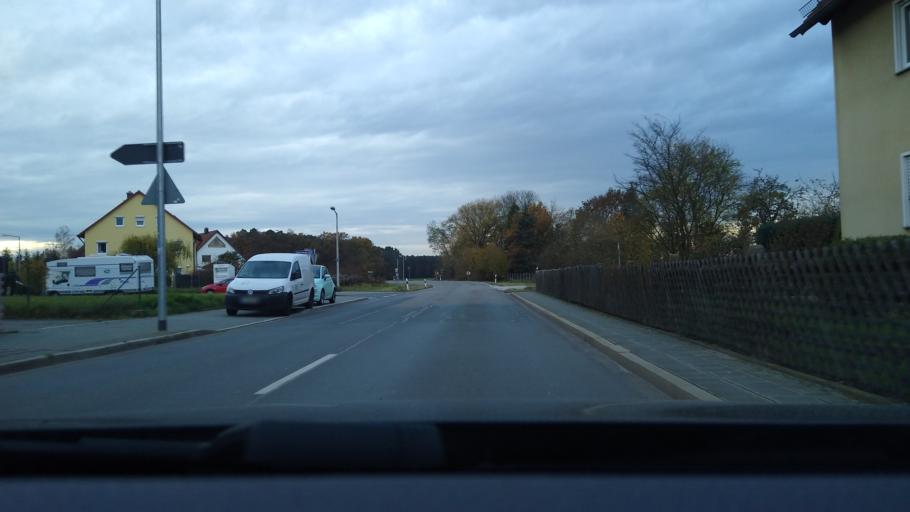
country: DE
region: Bavaria
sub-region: Regierungsbezirk Mittelfranken
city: Wendelstein
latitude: 49.3569
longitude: 11.0964
